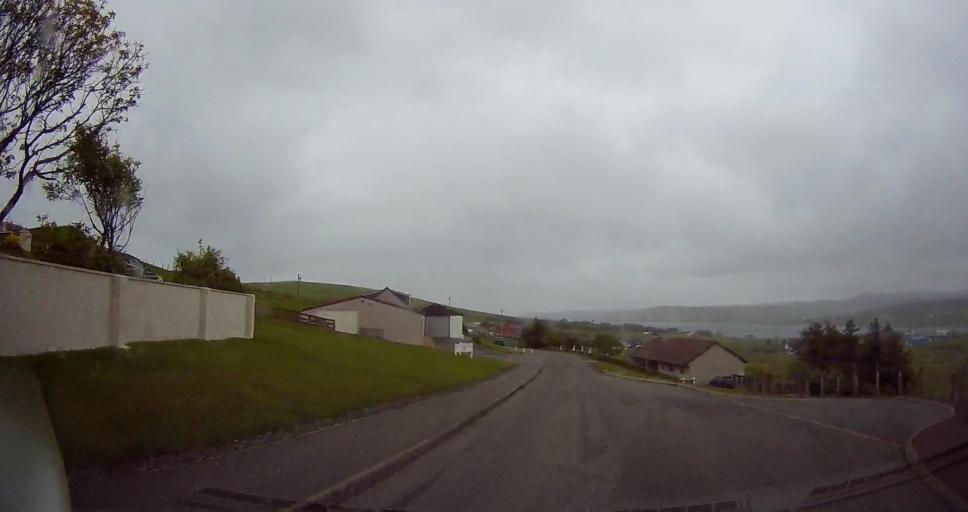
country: GB
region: Scotland
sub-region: Shetland Islands
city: Lerwick
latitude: 60.2798
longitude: -1.3890
